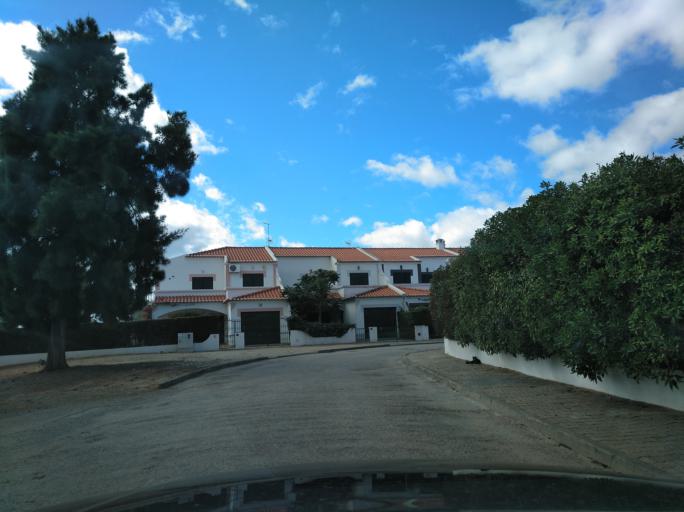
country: PT
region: Faro
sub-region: Vila Real de Santo Antonio
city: Monte Gordo
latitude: 37.1704
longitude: -7.5037
